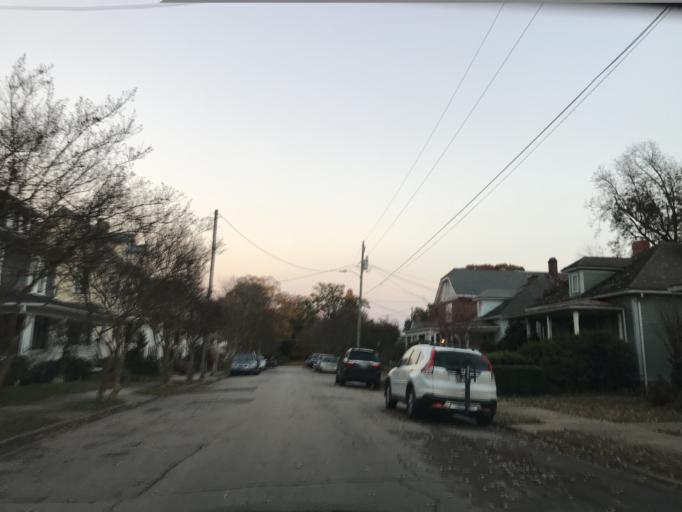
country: US
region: North Carolina
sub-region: Wake County
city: West Raleigh
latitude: 35.7913
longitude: -78.6485
